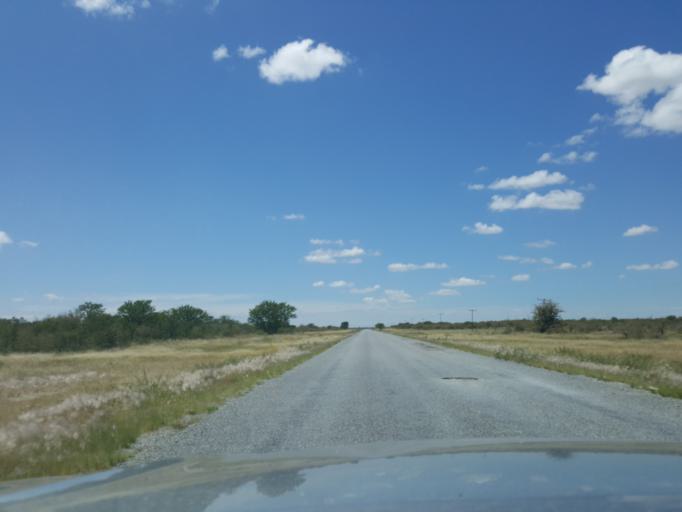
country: BW
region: Central
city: Gweta
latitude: -20.1363
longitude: 25.6593
